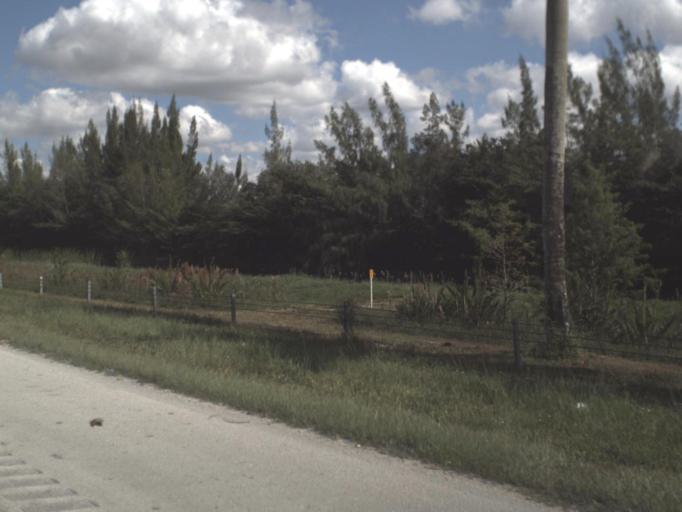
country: US
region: Florida
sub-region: Miami-Dade County
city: Palm Springs North
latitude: 25.9203
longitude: -80.3781
